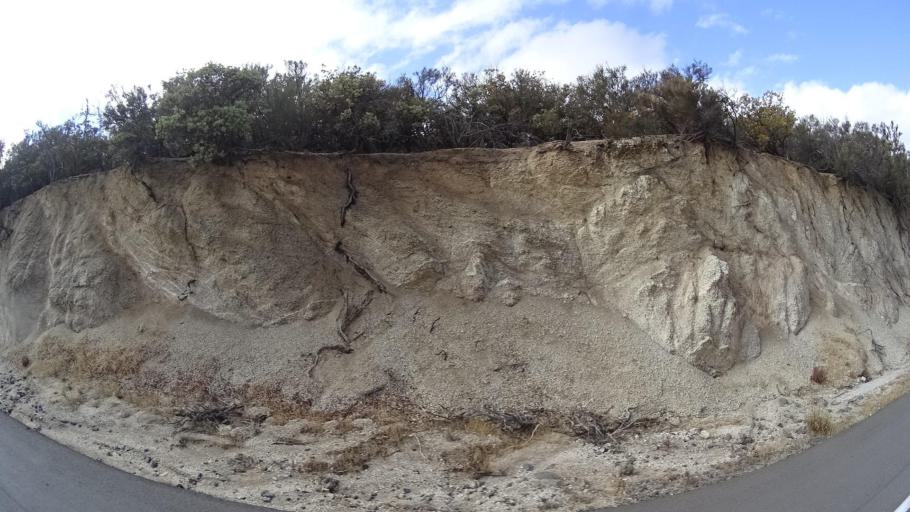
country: US
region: California
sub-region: San Diego County
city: Campo
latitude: 32.7216
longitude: -116.4094
